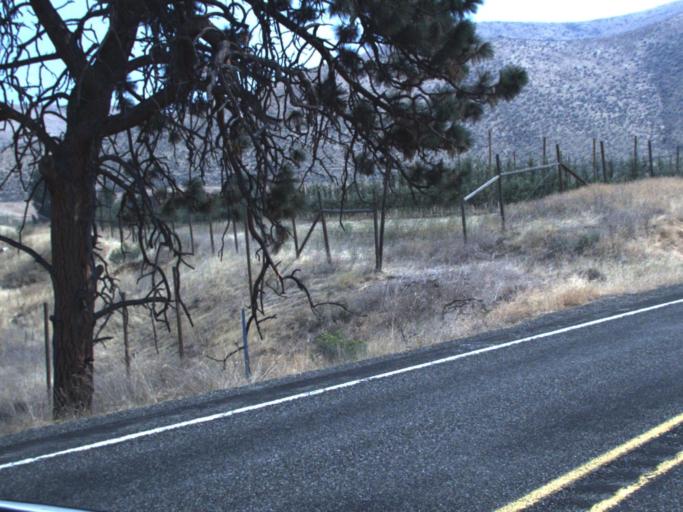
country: US
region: Washington
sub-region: Kittitas County
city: Ellensburg
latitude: 46.9035
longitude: -120.4937
